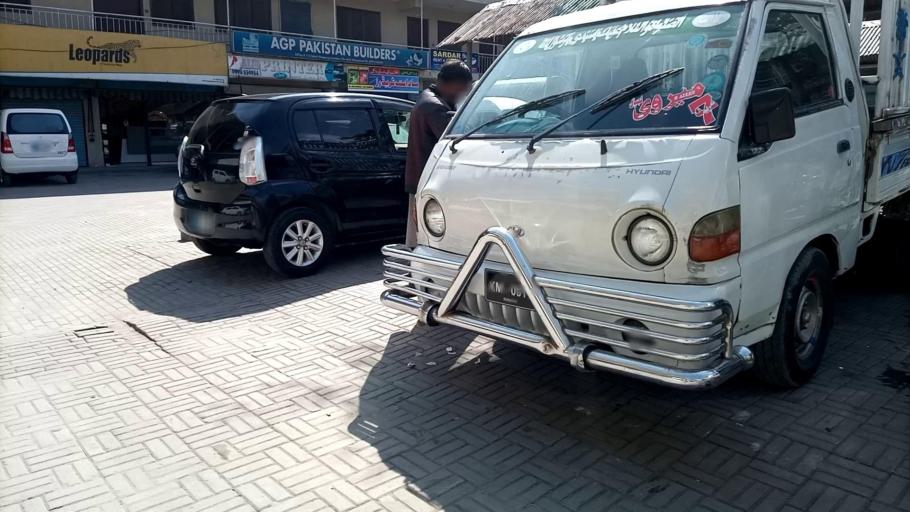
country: PK
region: Khyber Pakhtunkhwa
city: Abbottabad
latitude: 34.1435
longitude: 73.2150
